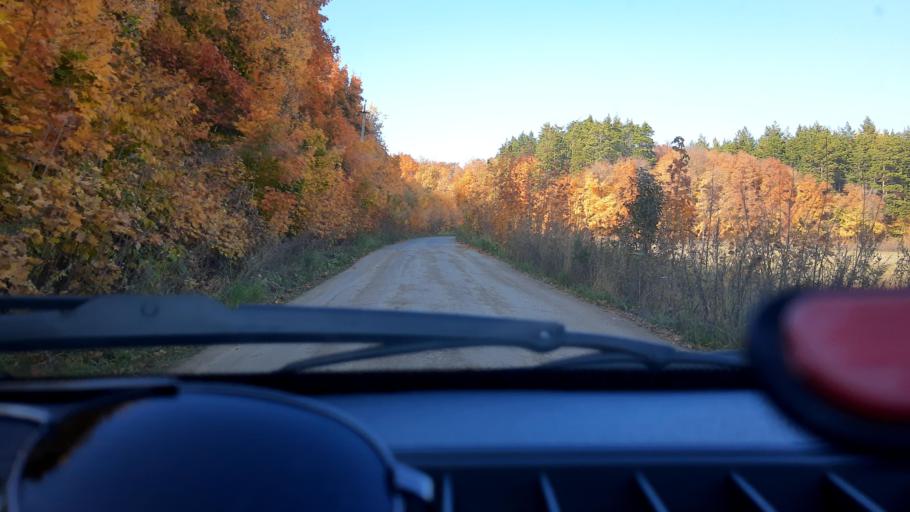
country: RU
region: Bashkortostan
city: Karmaskaly
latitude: 54.3764
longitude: 55.9104
